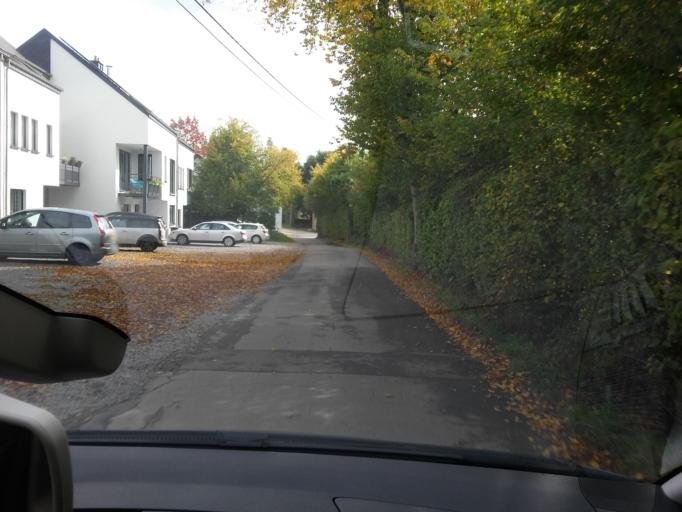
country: BE
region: Wallonia
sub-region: Province du Luxembourg
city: Arlon
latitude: 49.6989
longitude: 5.7940
